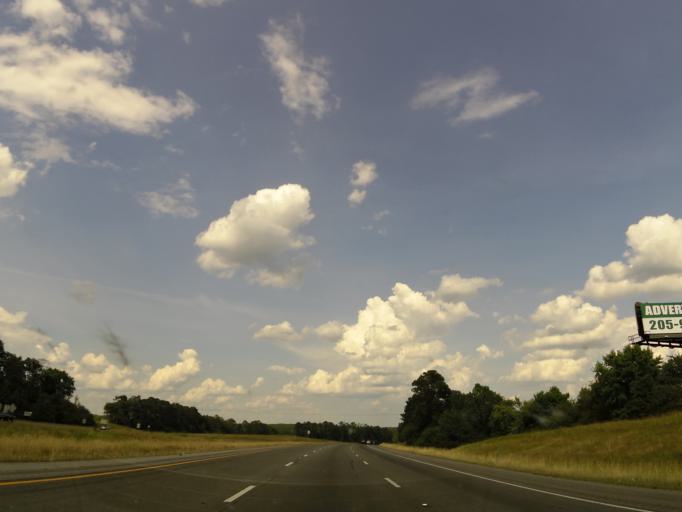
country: US
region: Alabama
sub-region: Tuscaloosa County
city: Coaling
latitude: 33.1827
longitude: -87.3646
